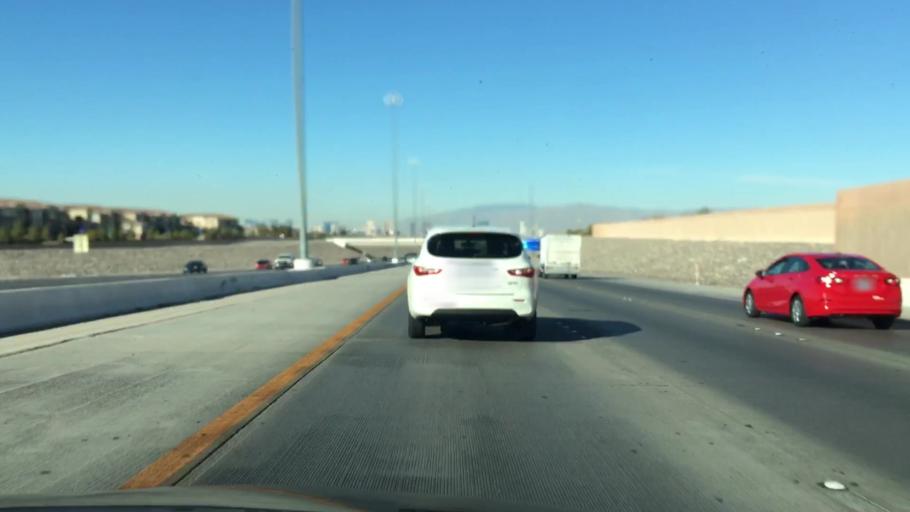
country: US
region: Nevada
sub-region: Clark County
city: Whitney
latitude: 36.0315
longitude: -115.1319
